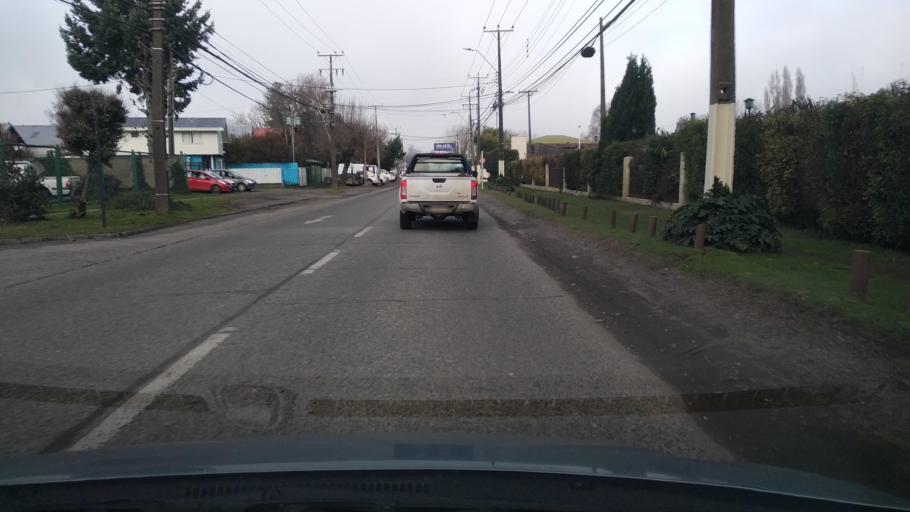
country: CL
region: Los Rios
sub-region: Provincia de Valdivia
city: Valdivia
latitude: -39.8071
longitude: -73.2362
